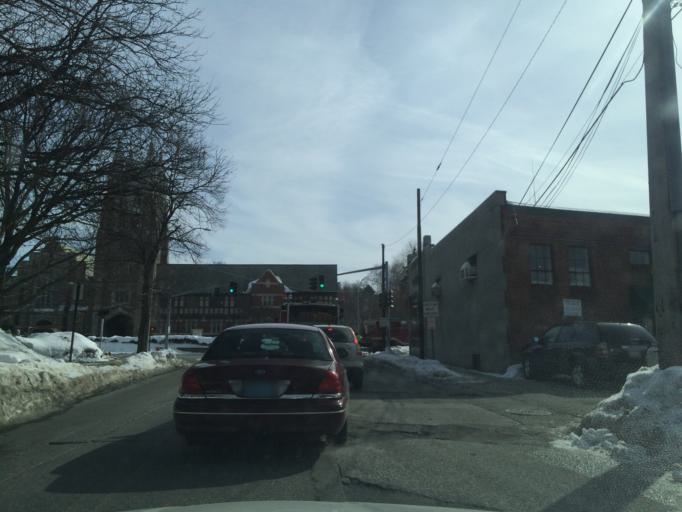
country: US
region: Massachusetts
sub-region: Middlesex County
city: Newton
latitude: 42.3495
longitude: -71.2284
